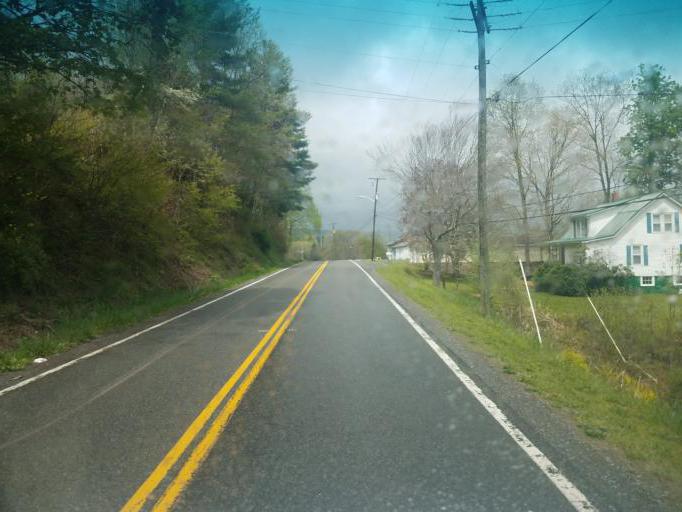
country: US
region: Virginia
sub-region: Bland County
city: Bland
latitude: 37.1567
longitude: -81.1500
